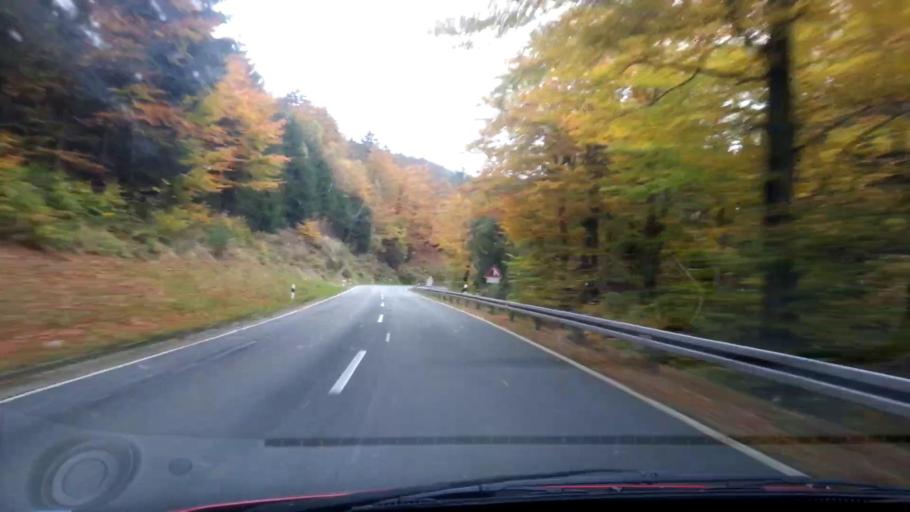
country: DE
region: Bavaria
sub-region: Upper Franconia
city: Warmensteinach
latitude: 49.9612
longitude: 11.7619
